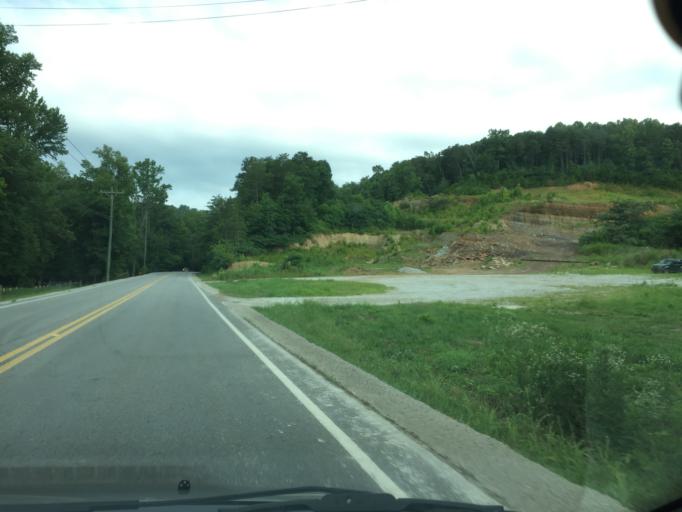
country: US
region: Tennessee
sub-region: Hamilton County
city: Apison
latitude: 34.9889
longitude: -85.0695
